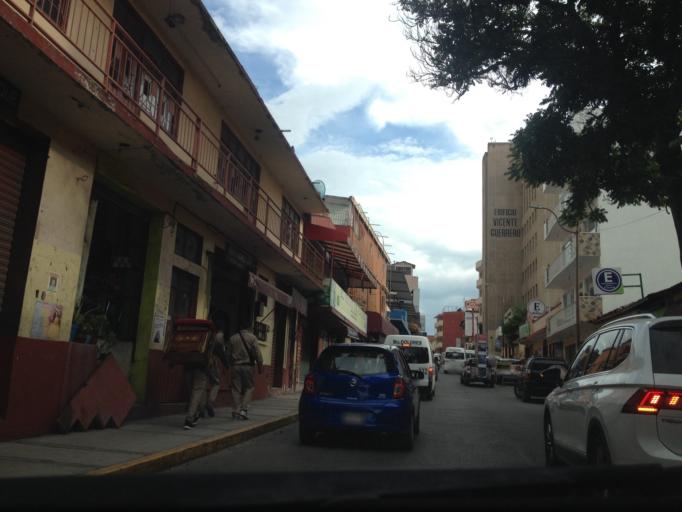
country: MX
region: Guerrero
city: Chilpancingo de los Bravos
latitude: 17.5538
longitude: -99.5032
